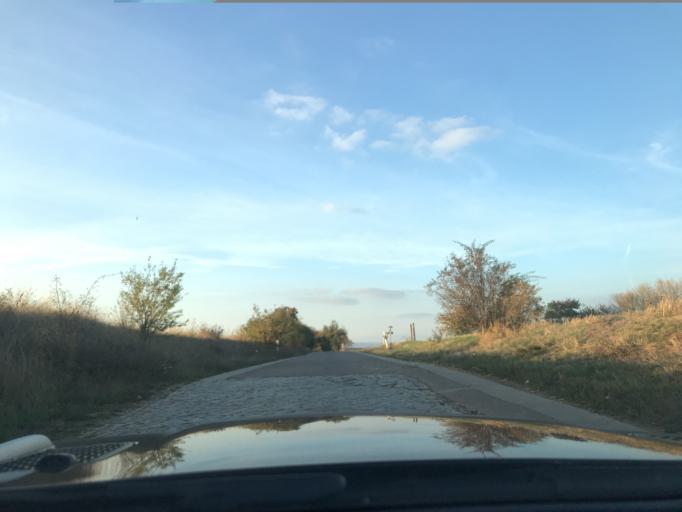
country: DE
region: Thuringia
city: Flarchheim
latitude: 51.1307
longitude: 10.4821
